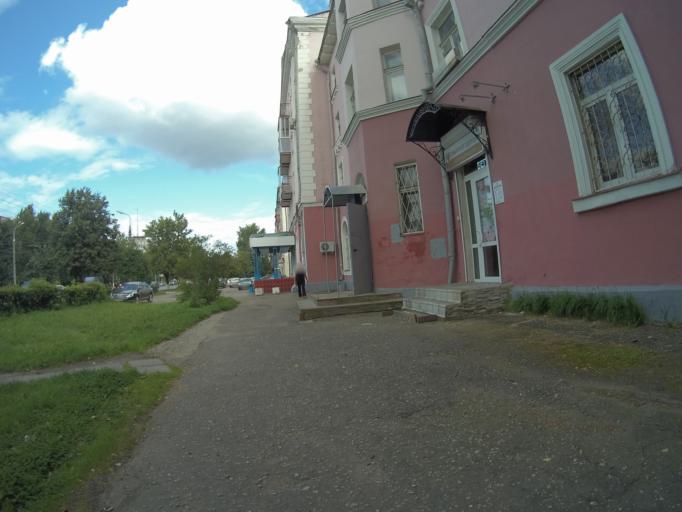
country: RU
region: Vladimir
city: Vladimir
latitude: 56.1212
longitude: 40.3788
